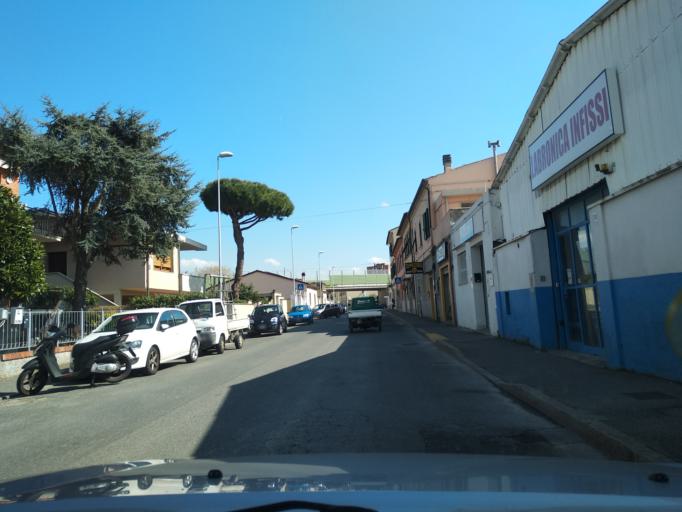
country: IT
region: Tuscany
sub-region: Provincia di Livorno
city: Livorno
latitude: 43.5429
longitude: 10.3377
